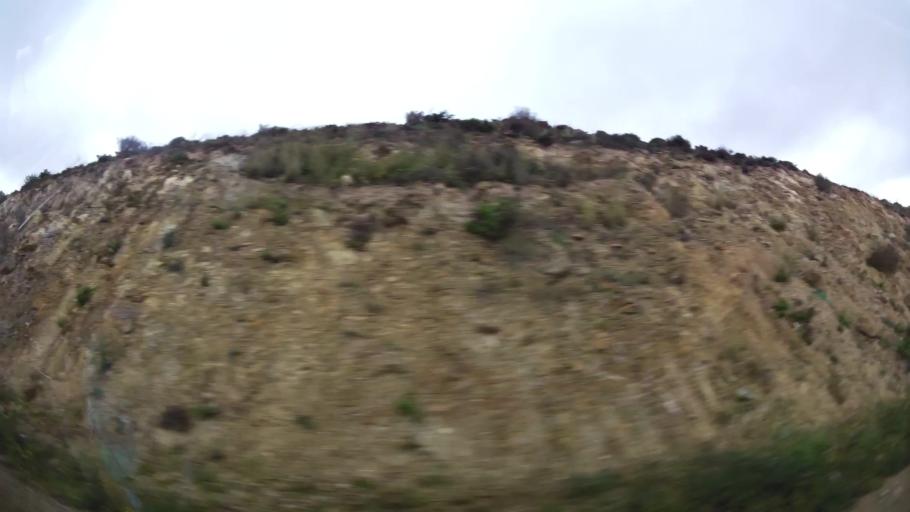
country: MA
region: Oriental
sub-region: Nador
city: Midar
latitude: 35.0667
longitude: -3.4799
